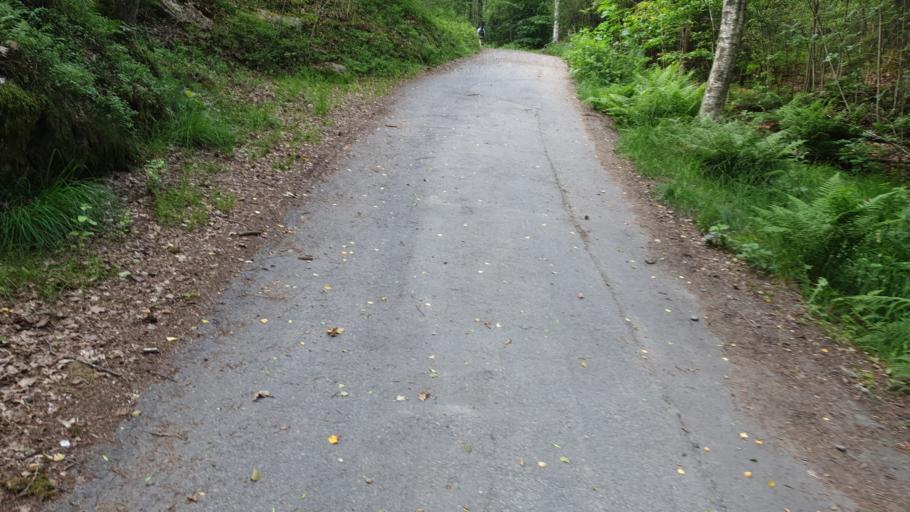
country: SE
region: Vaestra Goetaland
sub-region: Molndal
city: Moelndal
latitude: 57.6669
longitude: 12.0441
